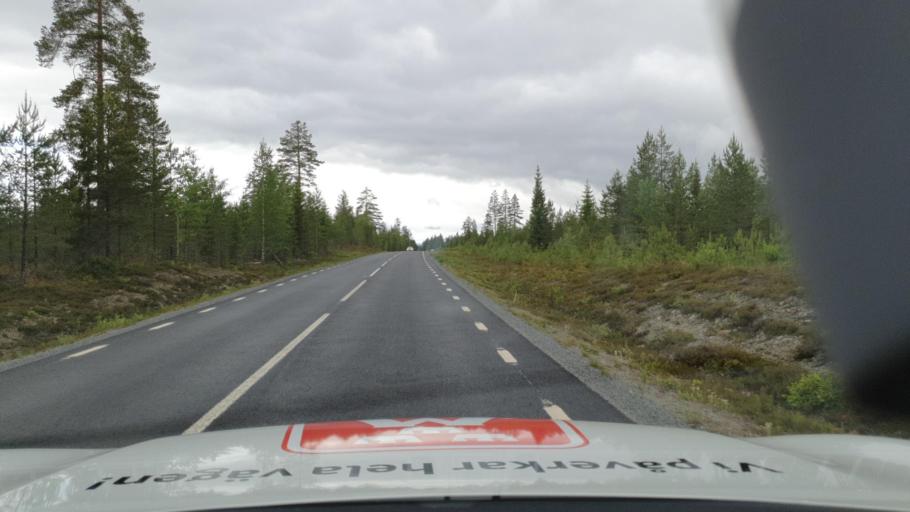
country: SE
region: Vaesterbotten
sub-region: Dorotea Kommun
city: Dorotea
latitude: 64.2077
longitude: 16.5597
